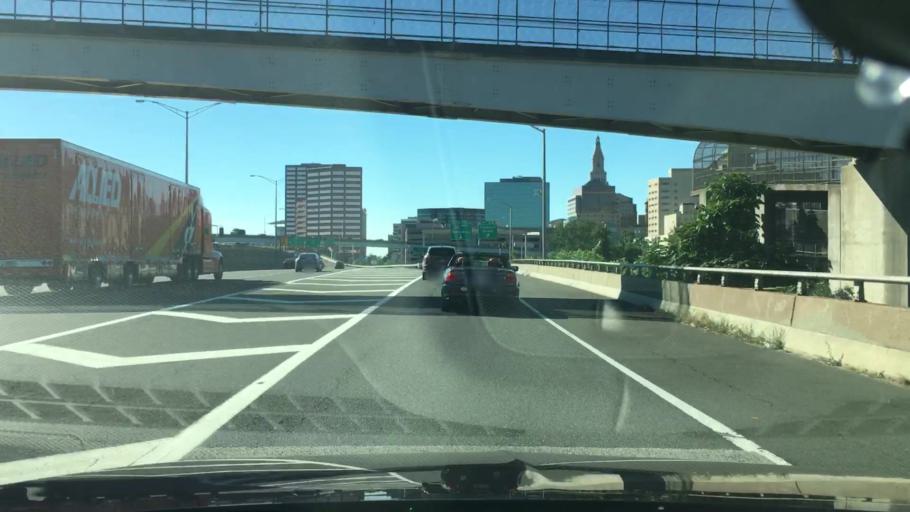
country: US
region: Connecticut
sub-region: Hartford County
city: Hartford
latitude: 41.7735
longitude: -72.6687
